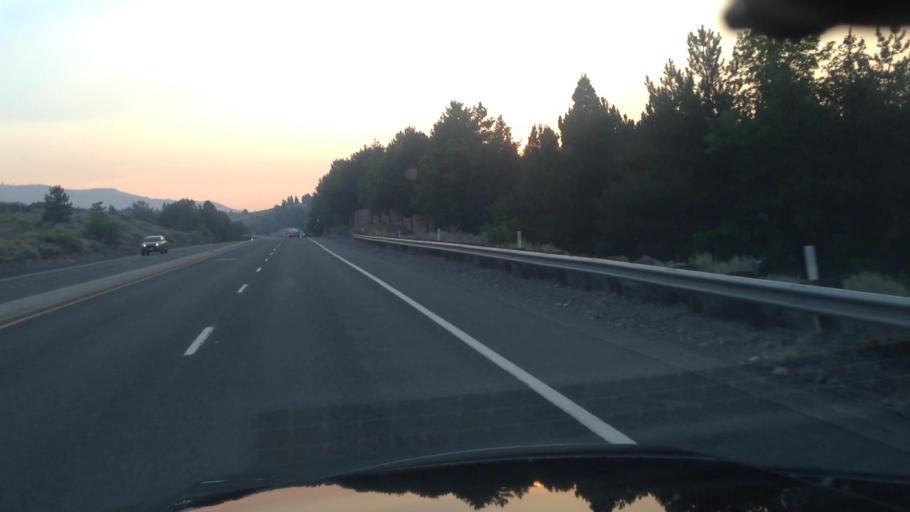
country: US
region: Nevada
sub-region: Washoe County
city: Reno
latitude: 39.4773
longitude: -119.8183
